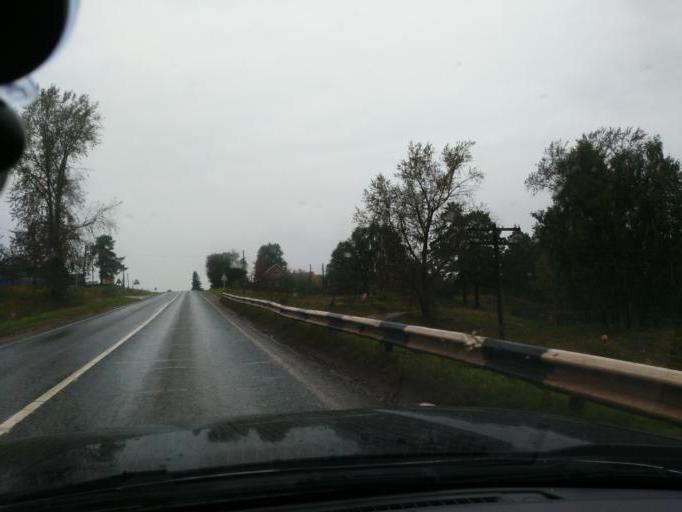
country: RU
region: Perm
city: Yugo-Kamskiy
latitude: 57.5541
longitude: 55.6856
